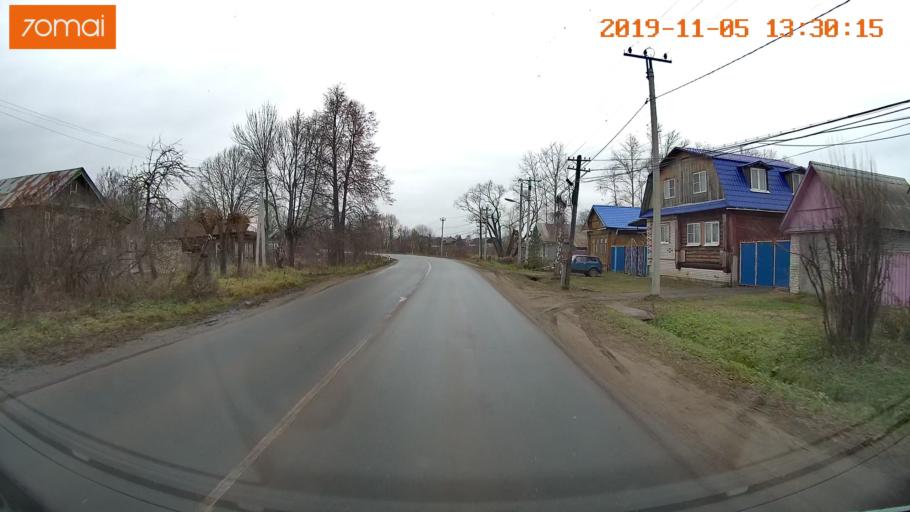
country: RU
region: Ivanovo
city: Shuya
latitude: 56.8656
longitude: 41.3968
